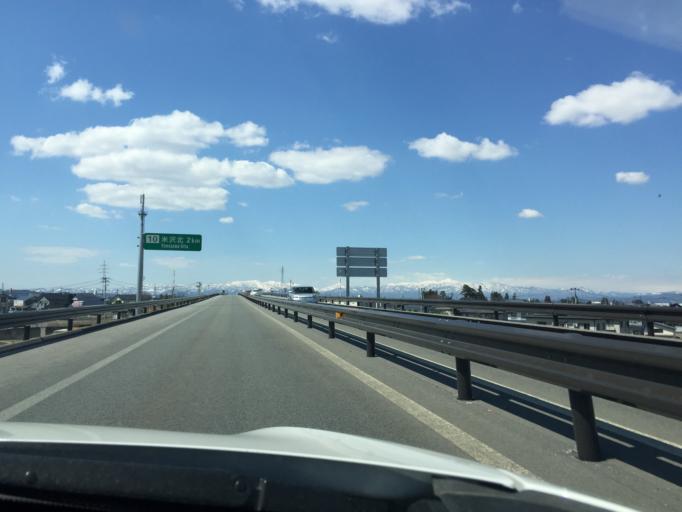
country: JP
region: Yamagata
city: Yonezawa
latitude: 37.9387
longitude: 140.1260
